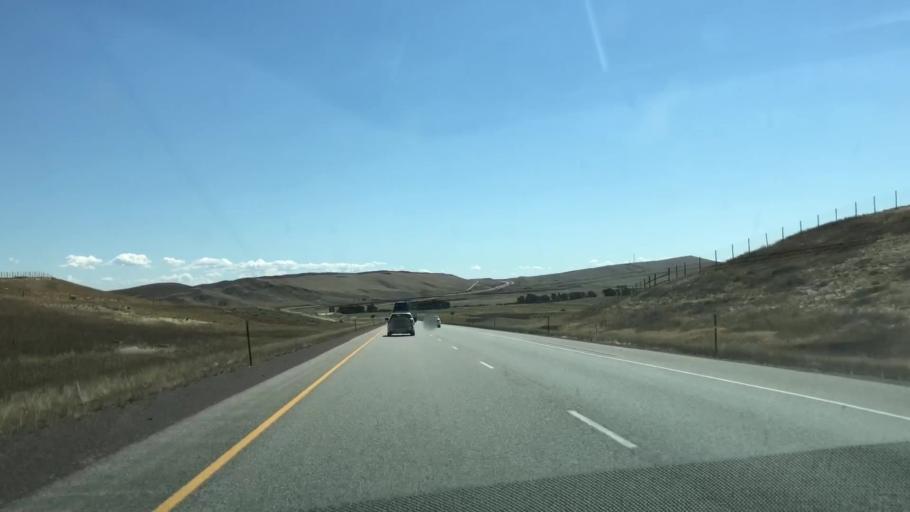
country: US
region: Wyoming
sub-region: Albany County
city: Laramie
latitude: 41.5332
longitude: -106.0737
